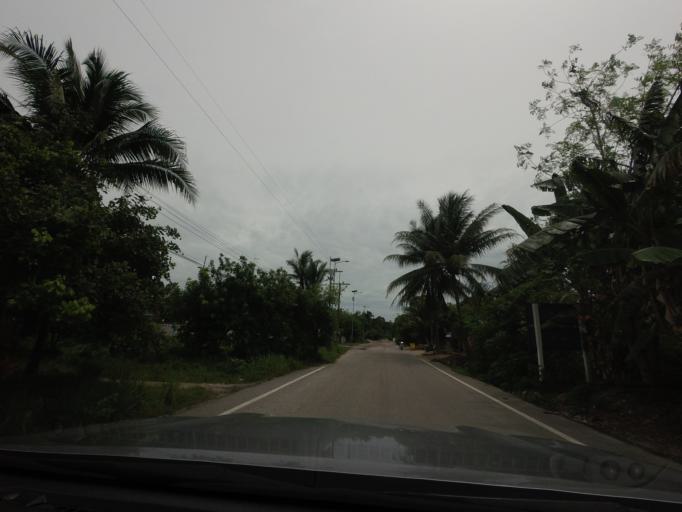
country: TH
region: Pattani
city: Sai Buri
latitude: 6.6525
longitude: 101.5541
